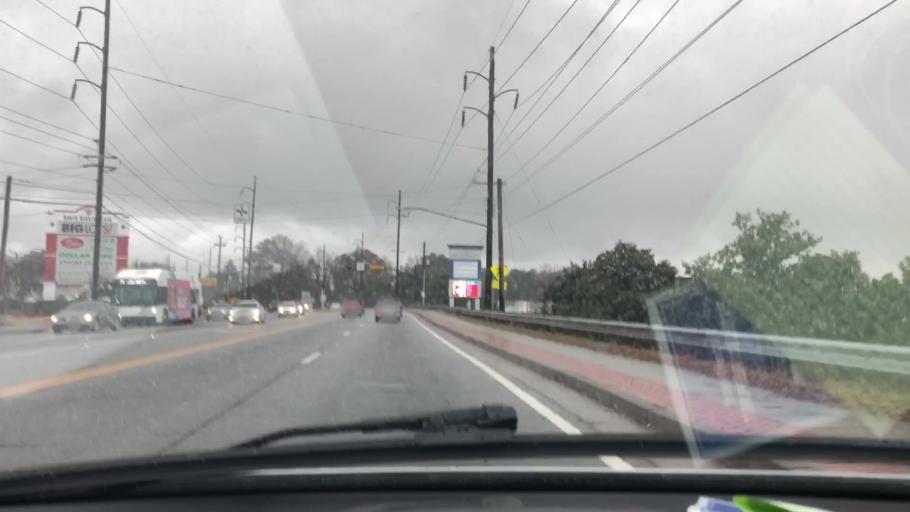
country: US
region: Georgia
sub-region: DeKalb County
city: Panthersville
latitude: 33.7095
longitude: -84.2720
